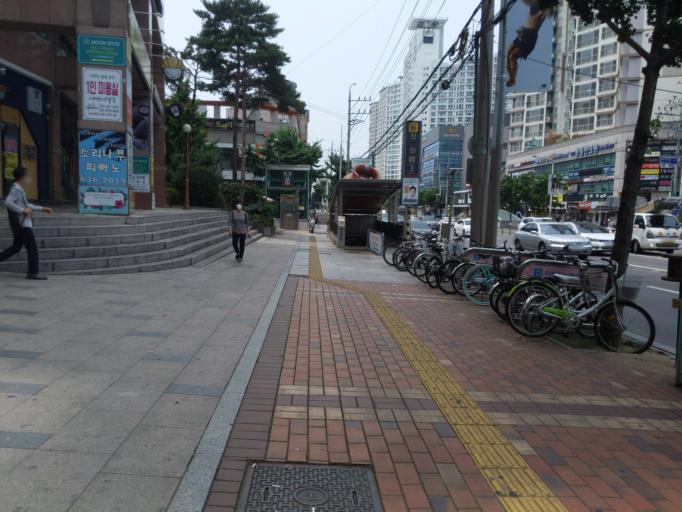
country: KR
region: Daegu
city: Hwawon
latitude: 35.8138
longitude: 128.5234
